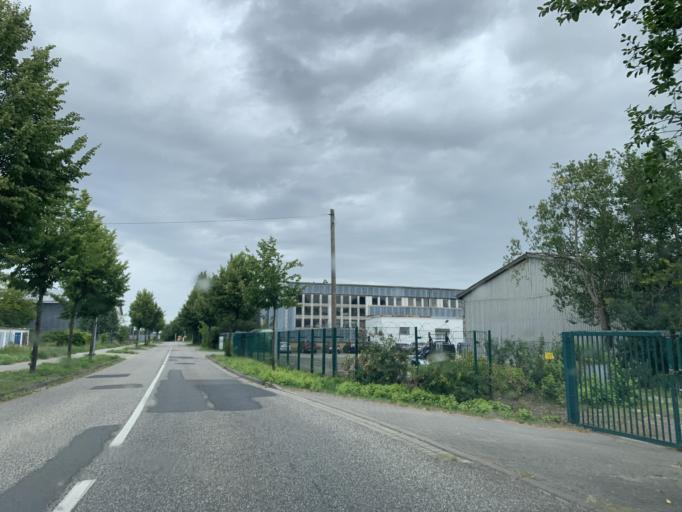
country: DE
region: Mecklenburg-Vorpommern
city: Neubrandenburg
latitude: 53.5213
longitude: 13.2717
